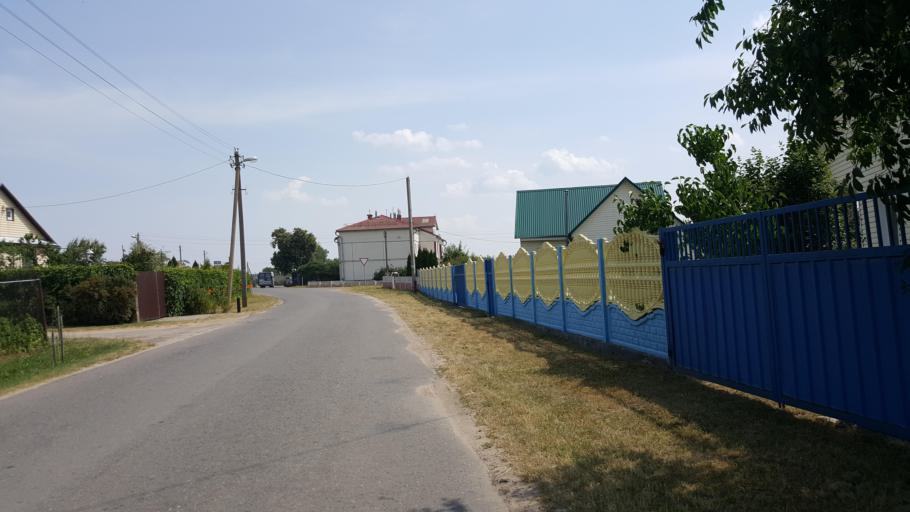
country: BY
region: Brest
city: Kamyanyets
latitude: 52.3267
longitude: 23.7807
